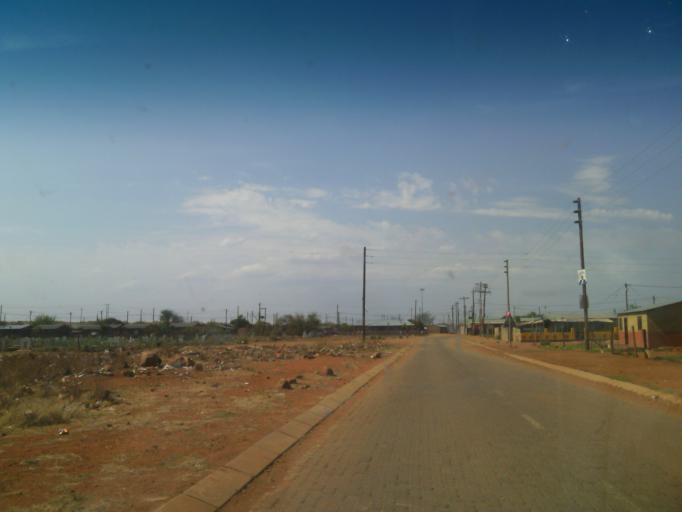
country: ZA
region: Northern Cape
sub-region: Frances Baard District Municipality
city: Barkly West
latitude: -28.5197
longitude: 24.5017
